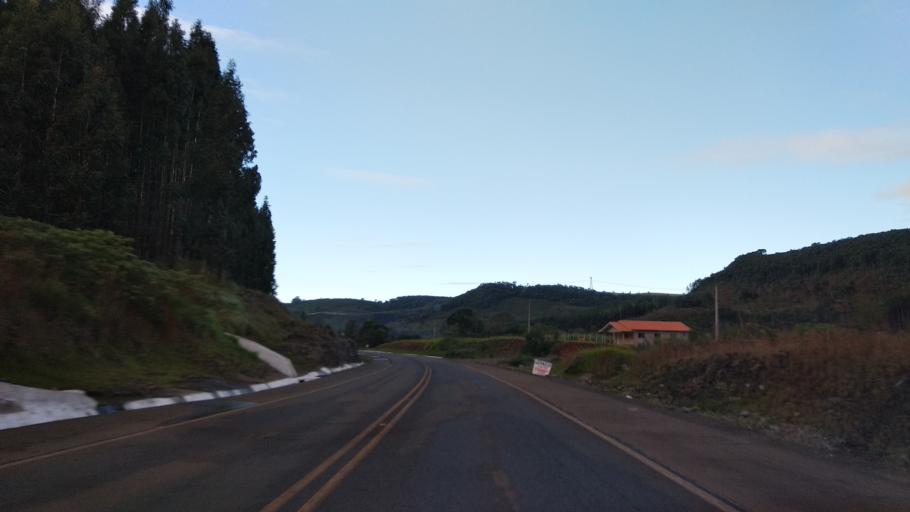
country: BR
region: Santa Catarina
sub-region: Curitibanos
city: Curitibanos
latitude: -27.5511
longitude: -50.8459
